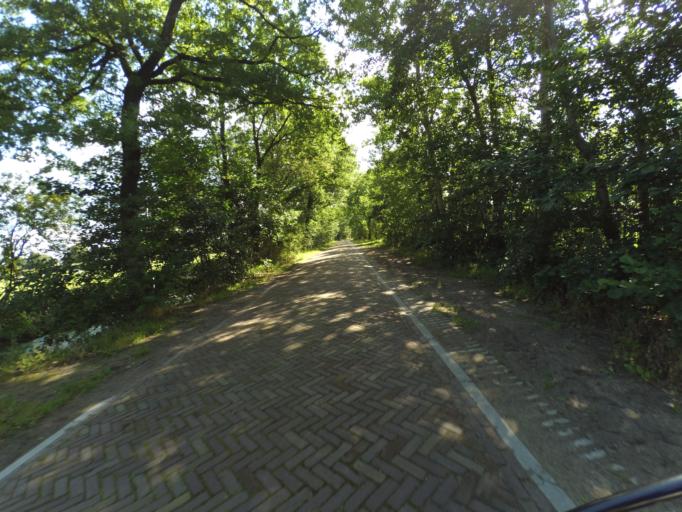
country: NL
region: Friesland
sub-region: Gemeente Tytsjerksteradiel
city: Noardburgum
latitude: 53.2048
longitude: 6.0099
